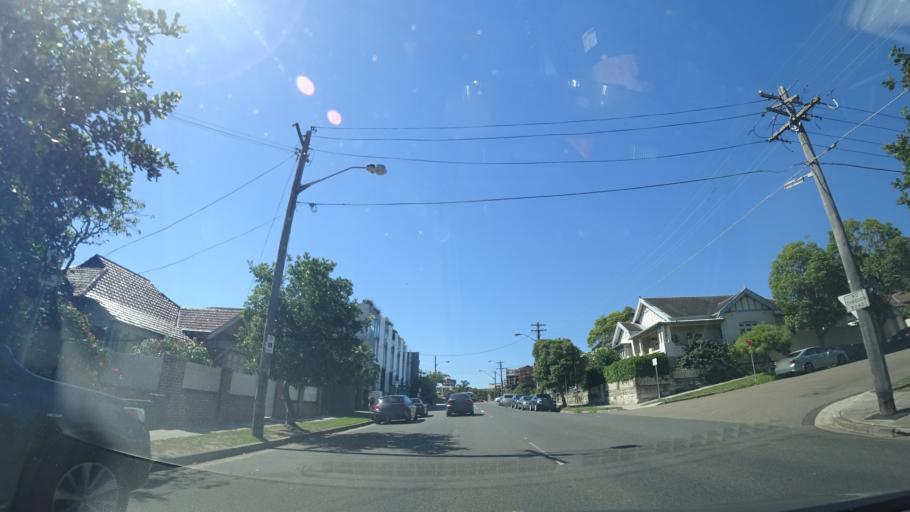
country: AU
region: New South Wales
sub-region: Randwick
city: Randwick
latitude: -33.9075
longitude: 151.2472
